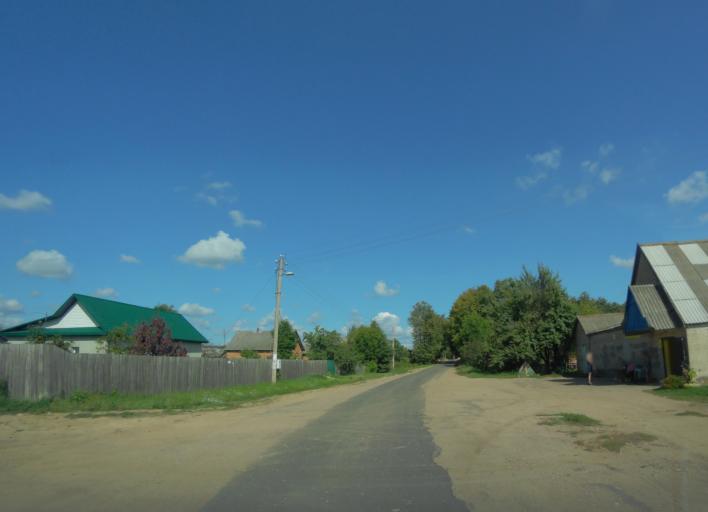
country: BY
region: Minsk
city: Zyembin
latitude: 54.3530
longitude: 28.3218
